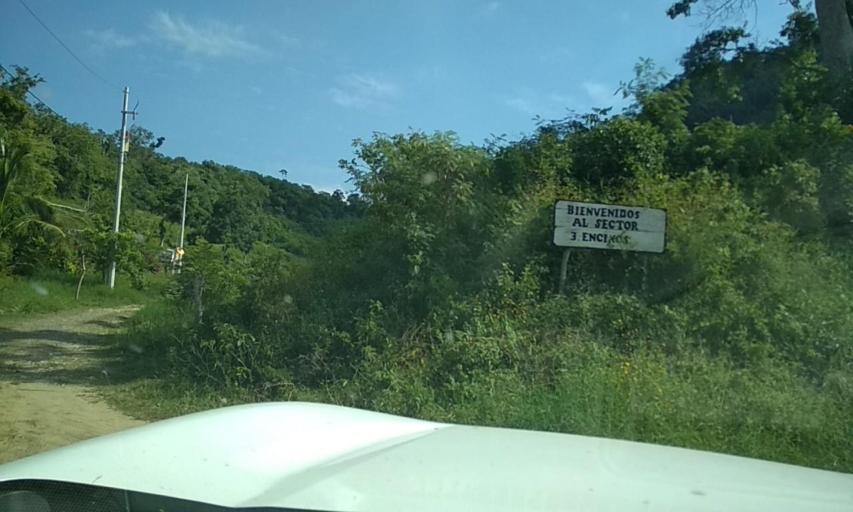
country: MX
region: Veracruz
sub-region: Cazones de Herrera
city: Rancho Nuevo
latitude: 20.6336
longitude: -97.2170
